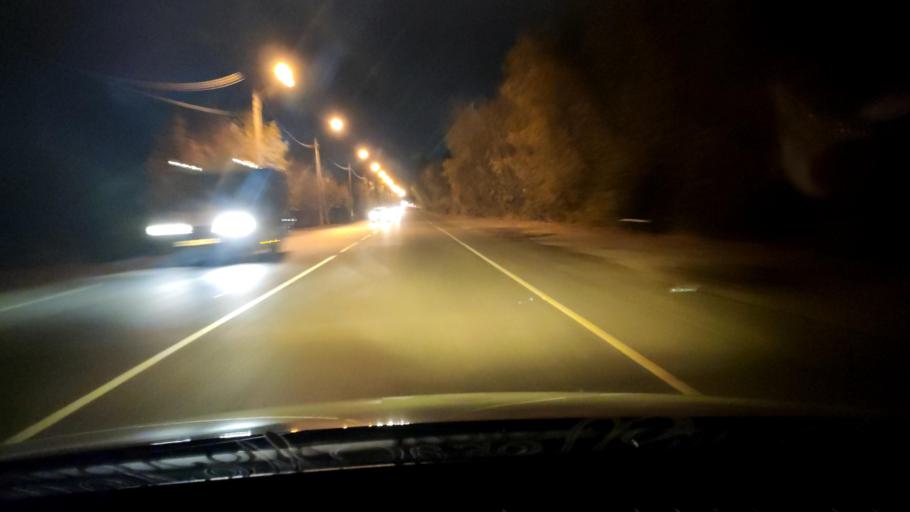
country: RU
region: Voronezj
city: Voronezh
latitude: 51.6024
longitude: 39.1777
